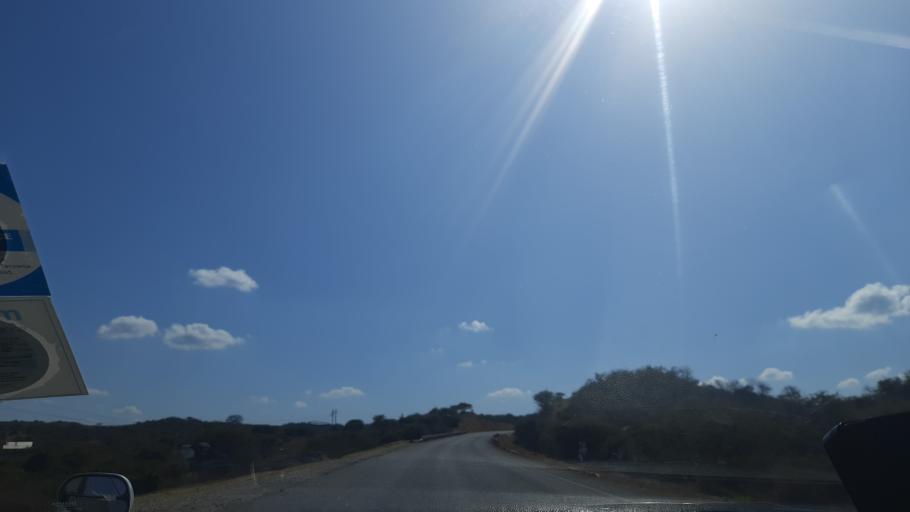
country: TZ
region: Singida
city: Kilimatinde
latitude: -5.7826
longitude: 34.8864
